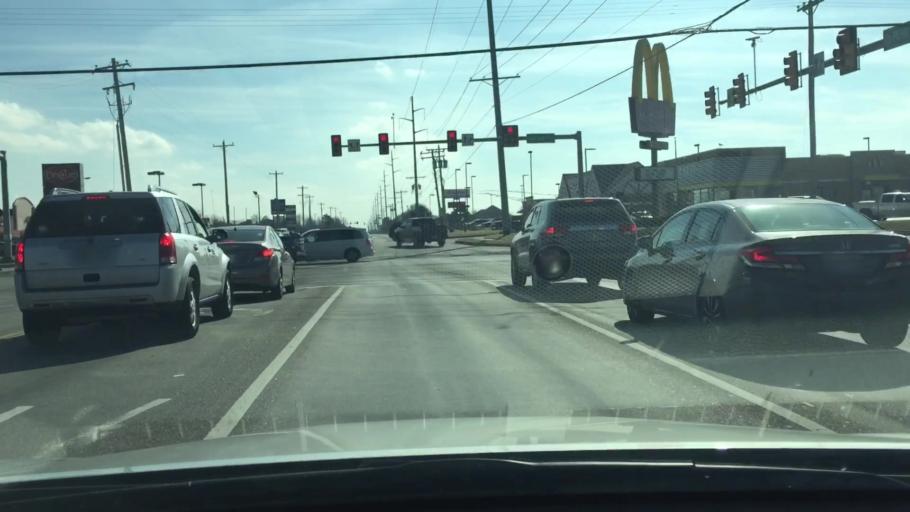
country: US
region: Oklahoma
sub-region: Cleveland County
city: Moore
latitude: 35.3775
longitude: -97.5479
